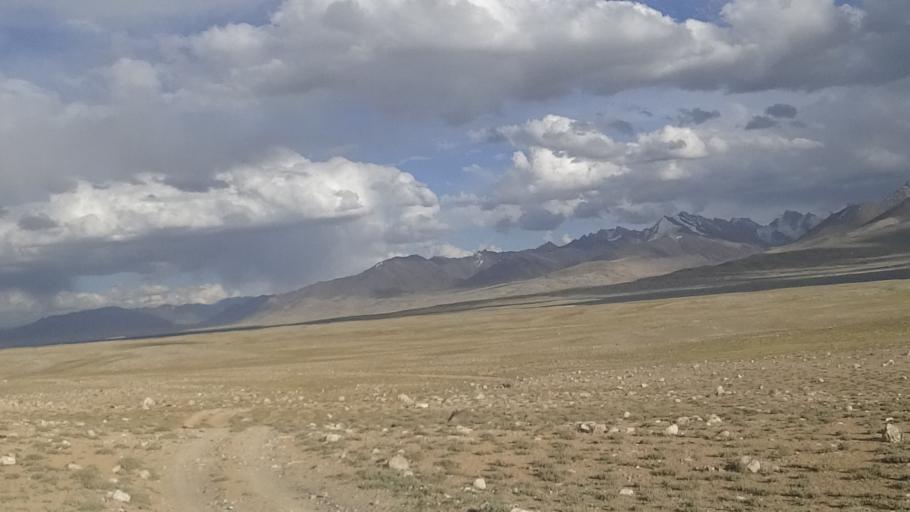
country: TJ
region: Gorno-Badakhshan
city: Murghob
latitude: 37.4626
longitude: 73.6155
